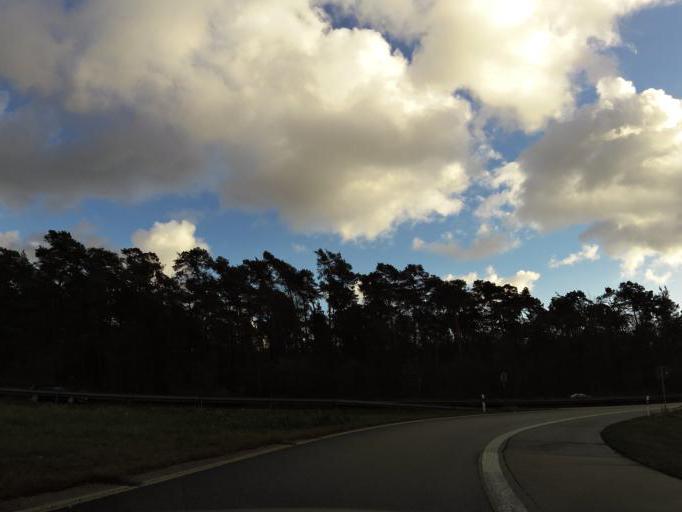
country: DE
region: Hesse
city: Raunheim
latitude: 49.9923
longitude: 8.4686
